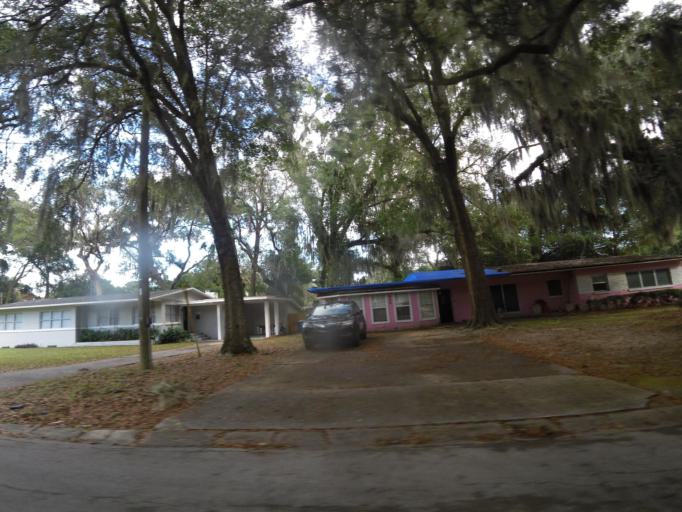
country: US
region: Florida
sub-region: Duval County
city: Jacksonville
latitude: 30.3249
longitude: -81.5914
